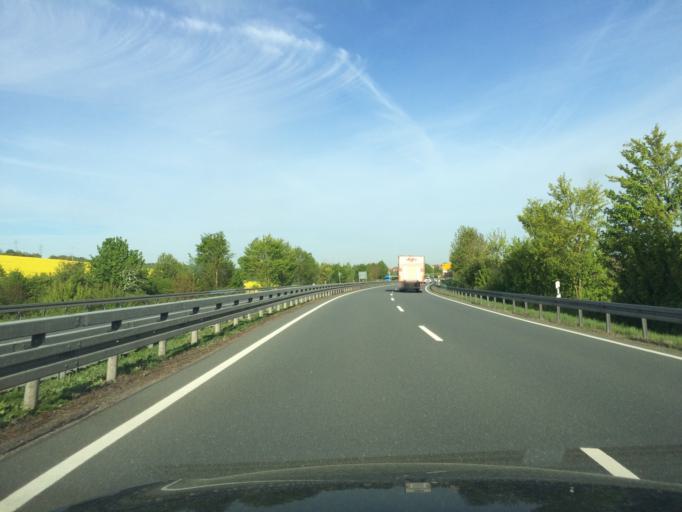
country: DE
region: Bavaria
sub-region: Regierungsbezirk Unterfranken
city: Rottendorf
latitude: 49.7831
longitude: 10.0400
